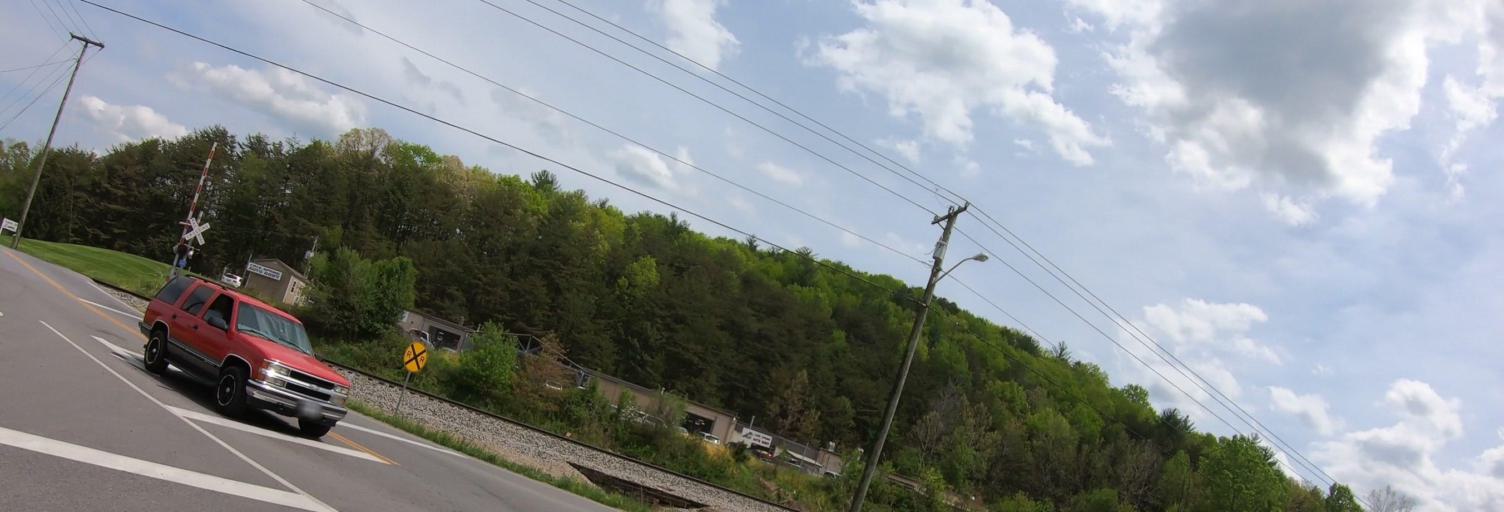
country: US
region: Virginia
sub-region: Roanoke County
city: Cave Spring
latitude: 37.2005
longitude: -80.0004
